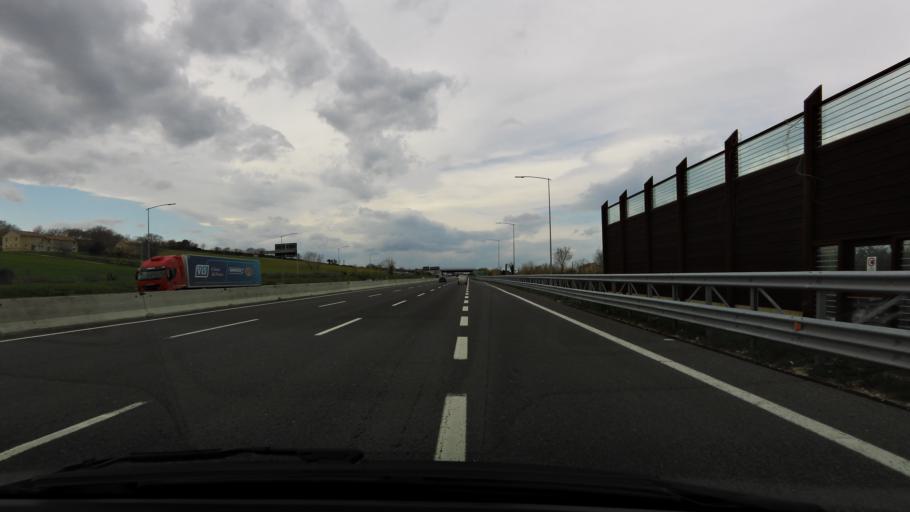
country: IT
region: The Marches
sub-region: Provincia di Pesaro e Urbino
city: Marotta
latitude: 43.7637
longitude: 13.1290
